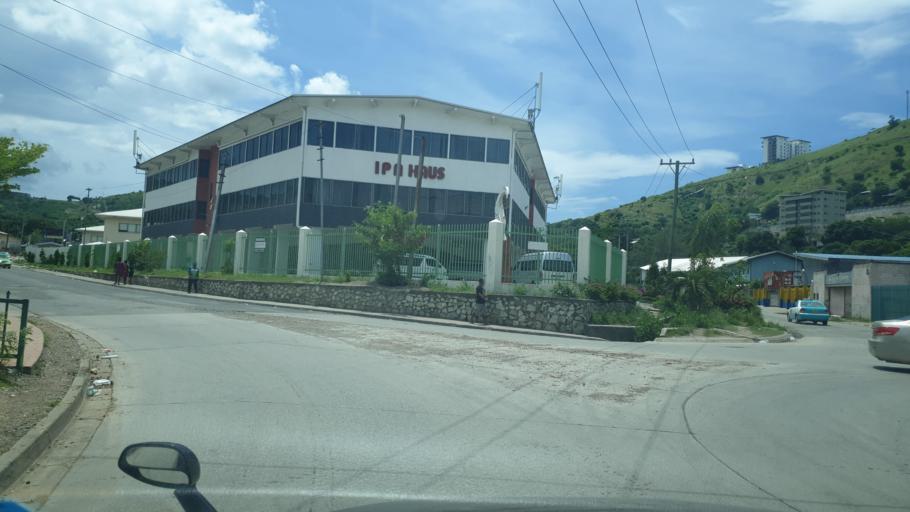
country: PG
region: National Capital
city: Port Moresby
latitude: -9.4670
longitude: 147.1582
